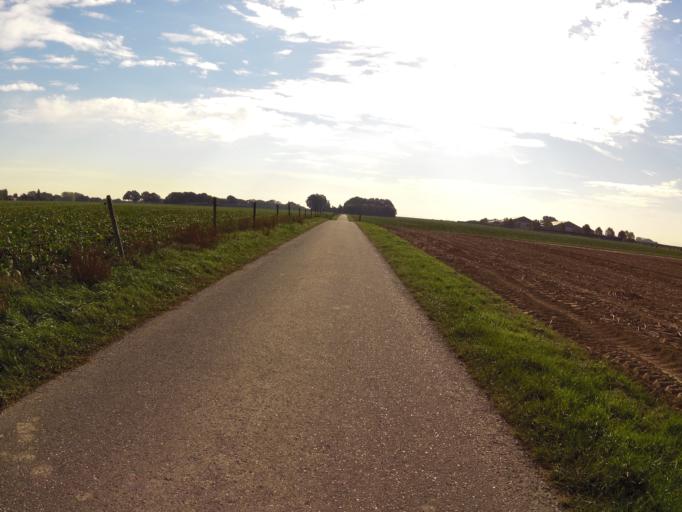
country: NL
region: Limburg
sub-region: Gemeente Schinnen
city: Doenrade
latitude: 50.9639
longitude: 5.8898
